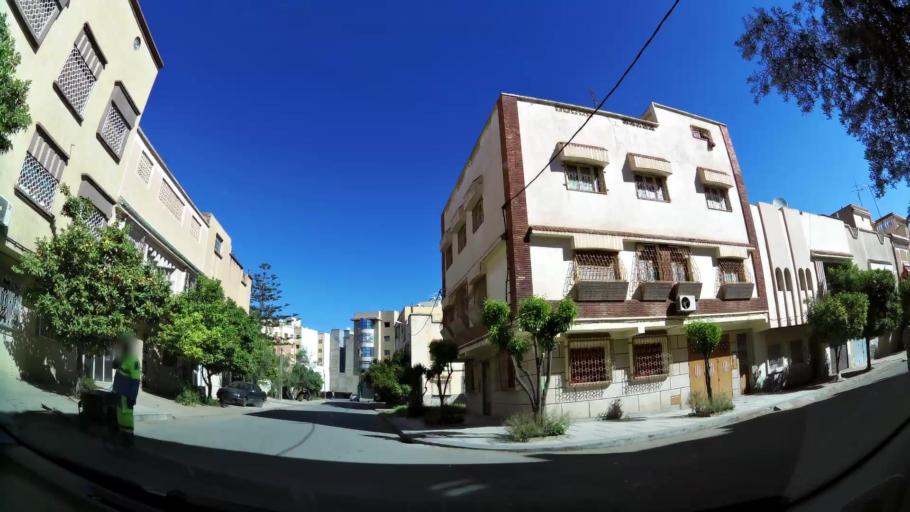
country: MA
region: Oriental
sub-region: Oujda-Angad
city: Oujda
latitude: 34.6563
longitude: -1.8967
